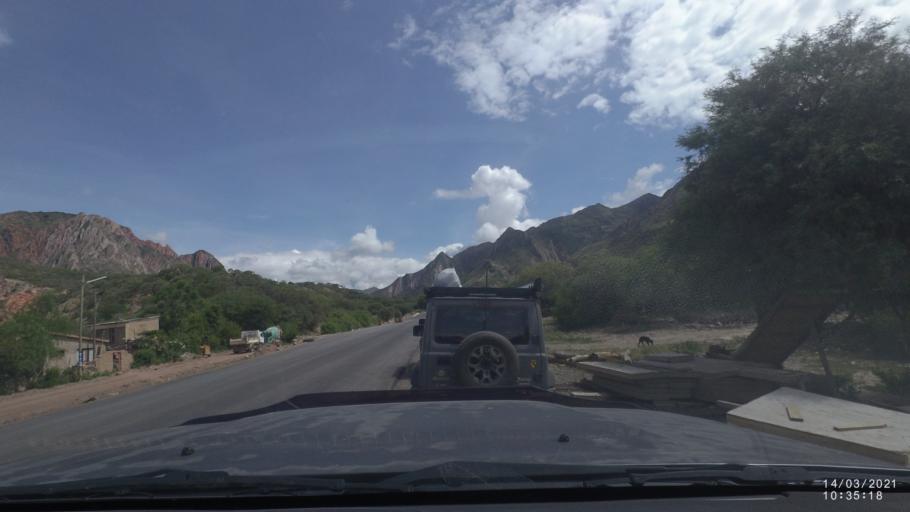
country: BO
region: Cochabamba
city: Cliza
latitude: -17.9081
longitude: -65.8799
